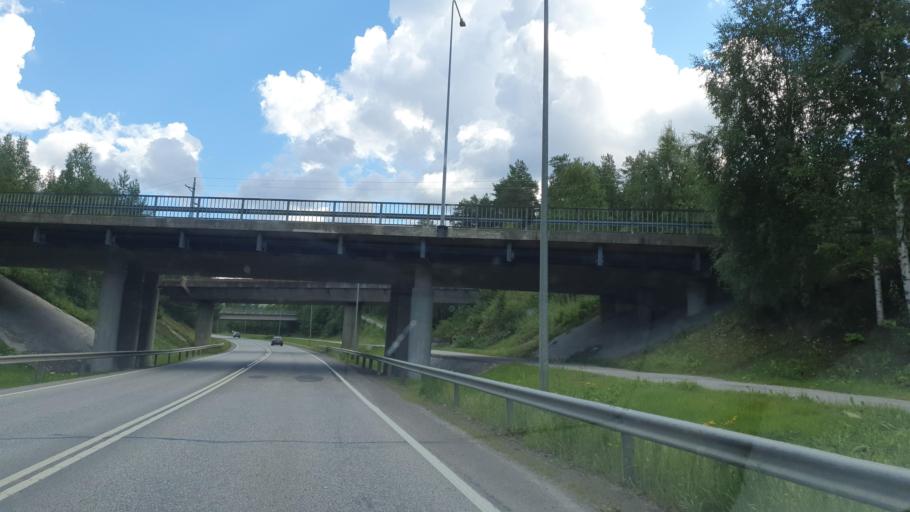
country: FI
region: Kainuu
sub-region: Kajaani
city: Kajaani
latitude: 64.2177
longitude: 27.6977
